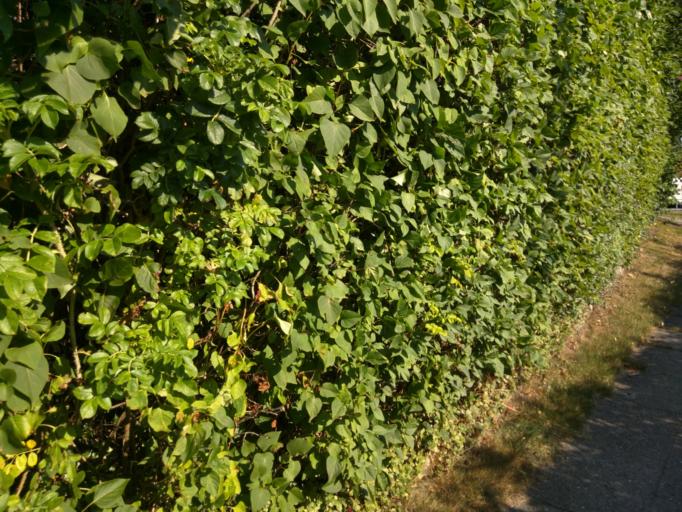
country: DK
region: Central Jutland
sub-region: Viborg Kommune
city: Viborg
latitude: 56.4331
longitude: 9.3999
